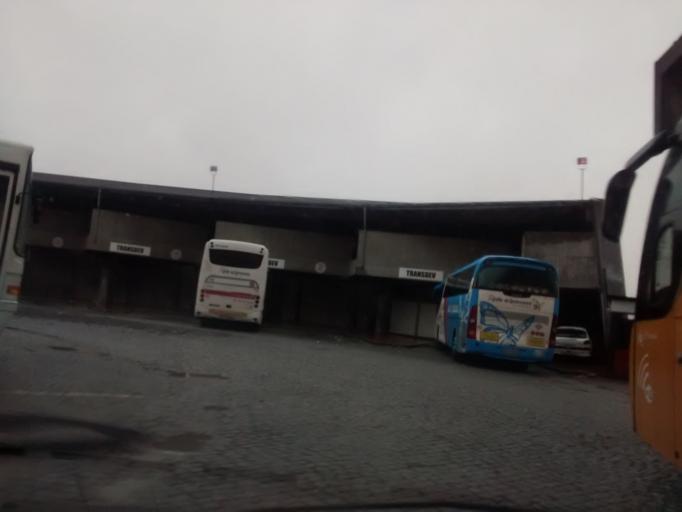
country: PT
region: Braga
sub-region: Braga
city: Braga
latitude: 41.5557
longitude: -8.4262
